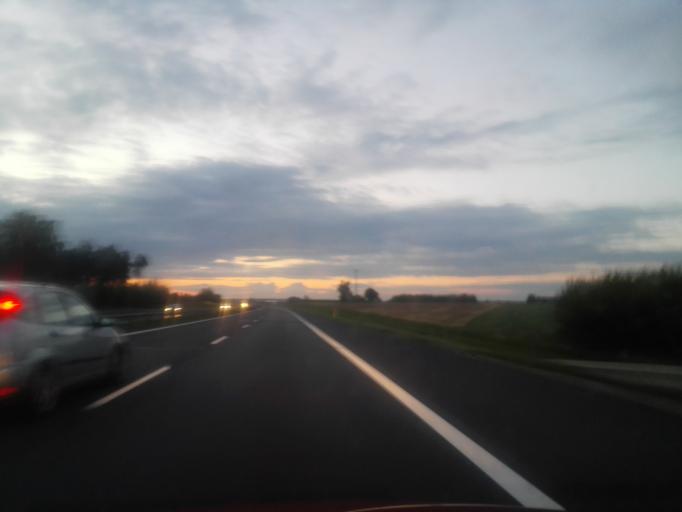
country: PL
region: Lodz Voivodeship
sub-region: Piotrkow Trybunalski
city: Piotrkow Trybunalski
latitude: 51.4508
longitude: 19.6415
